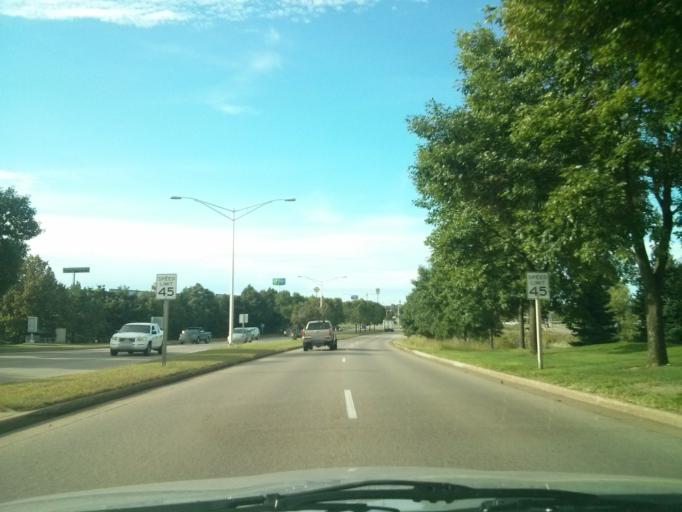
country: US
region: Wisconsin
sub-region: Saint Croix County
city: Hudson
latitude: 44.9548
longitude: -92.7211
